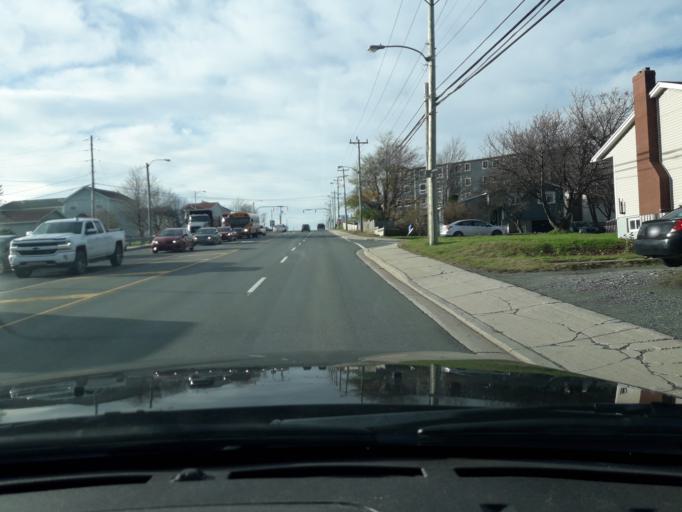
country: CA
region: Newfoundland and Labrador
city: St. John's
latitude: 47.5632
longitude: -52.7575
